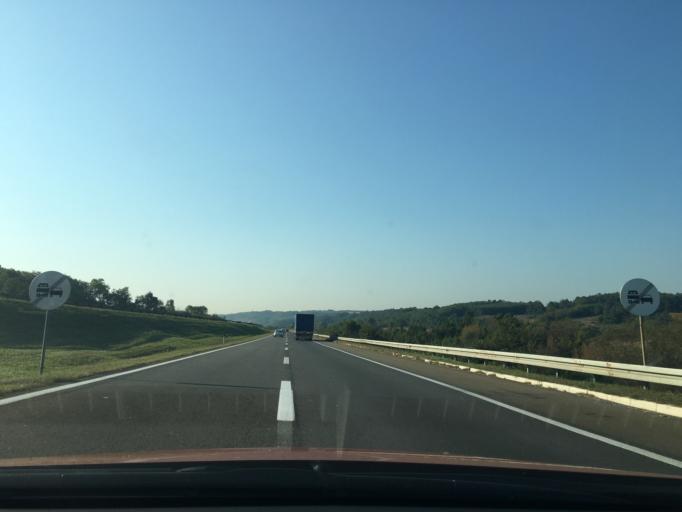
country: RS
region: Central Serbia
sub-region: Belgrade
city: Grocka
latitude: 44.6093
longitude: 20.6409
